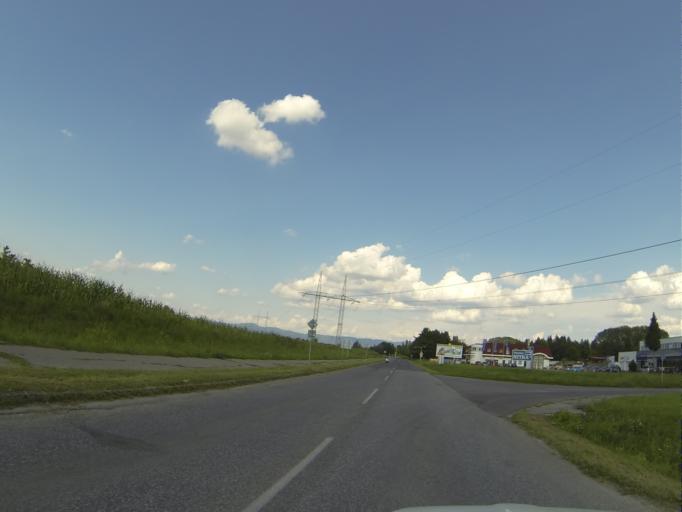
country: SK
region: Nitriansky
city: Bojnice
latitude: 48.7759
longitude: 18.5896
